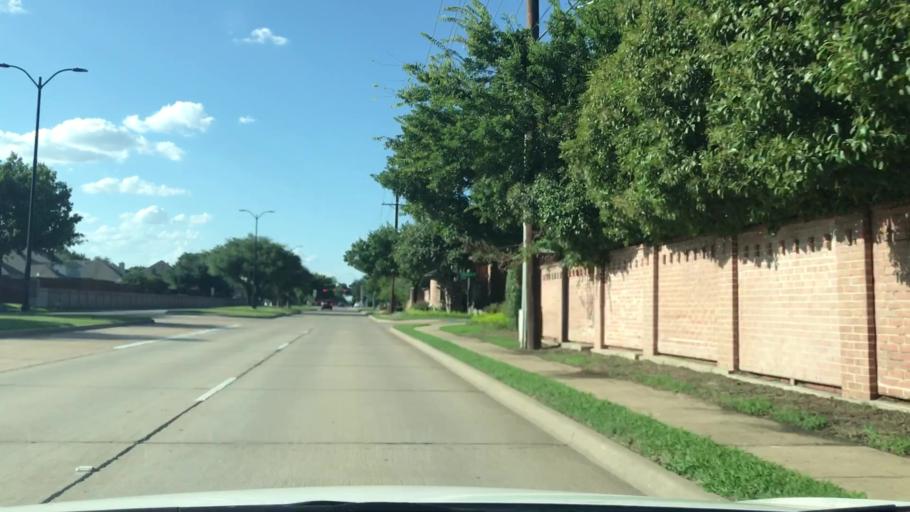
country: US
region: Texas
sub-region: Collin County
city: Frisco
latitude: 33.1138
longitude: -96.7880
